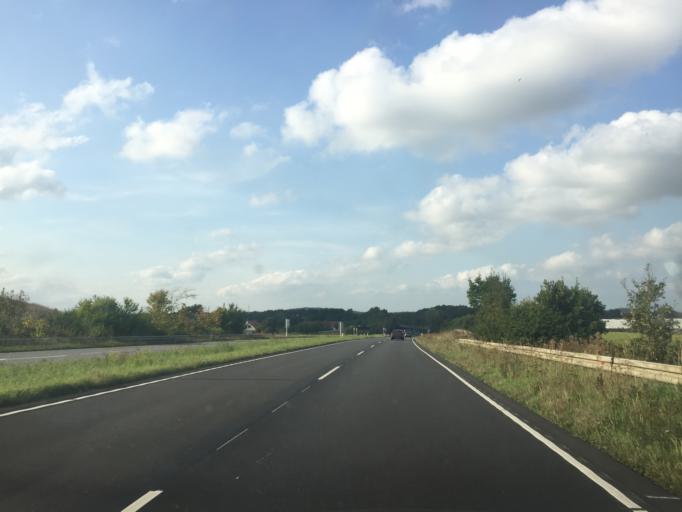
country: DK
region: Zealand
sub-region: Holbaek Kommune
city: Jyderup
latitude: 55.6530
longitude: 11.4312
